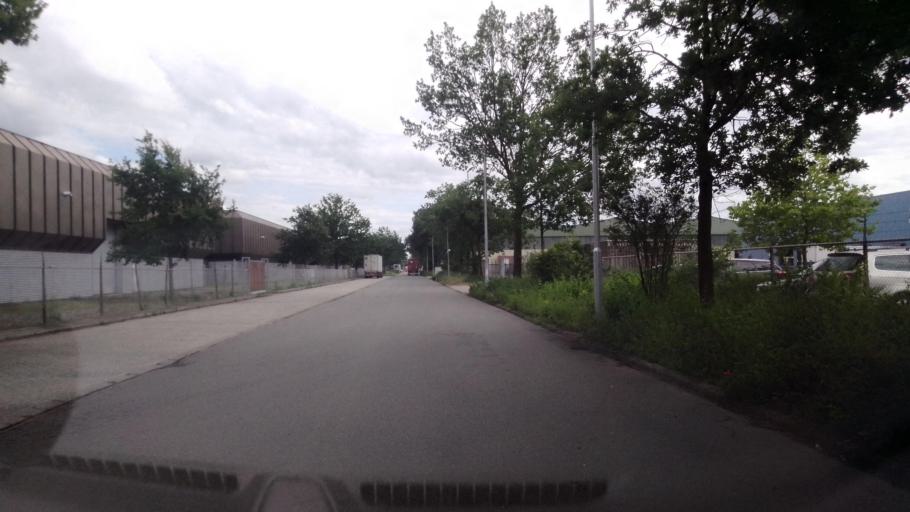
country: NL
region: Limburg
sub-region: Gemeente Venlo
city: Venlo
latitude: 51.3888
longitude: 6.1504
